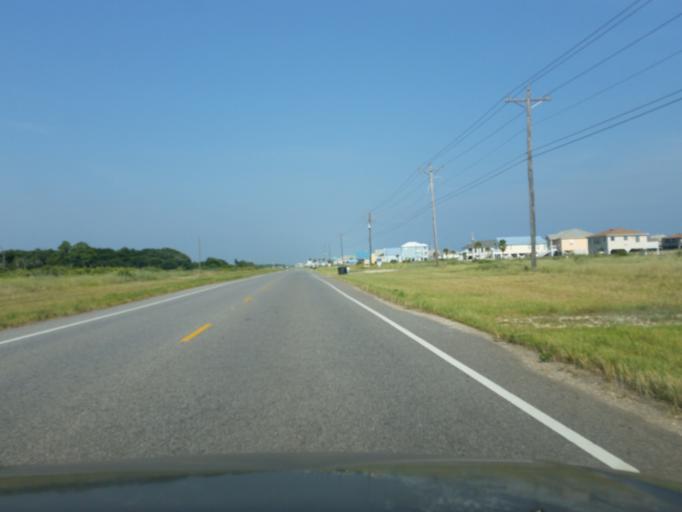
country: US
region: Alabama
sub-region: Mobile County
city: Dauphin Island
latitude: 30.2322
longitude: -87.9695
